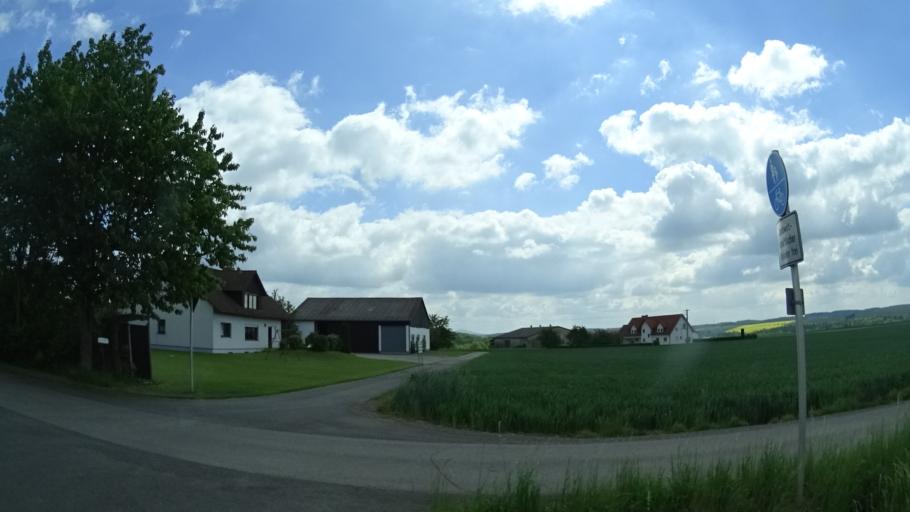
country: DE
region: Bavaria
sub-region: Regierungsbezirk Unterfranken
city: Mellrichstadt
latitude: 50.4560
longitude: 10.3166
